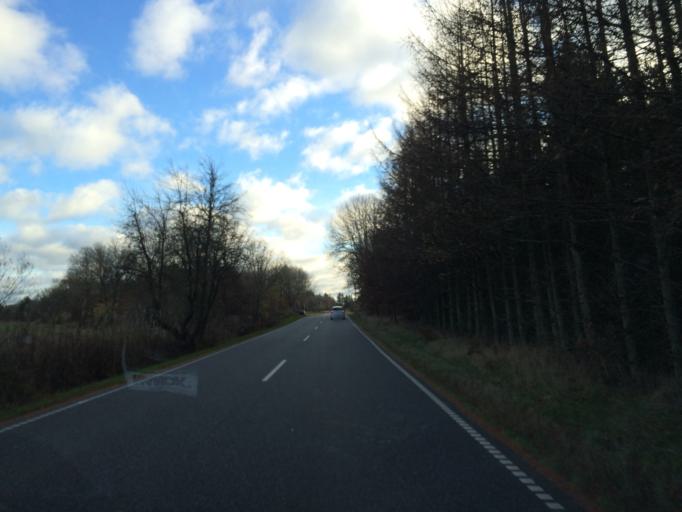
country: DK
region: Central Jutland
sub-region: Herning Kommune
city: Kibaek
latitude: 55.9339
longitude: 8.8957
